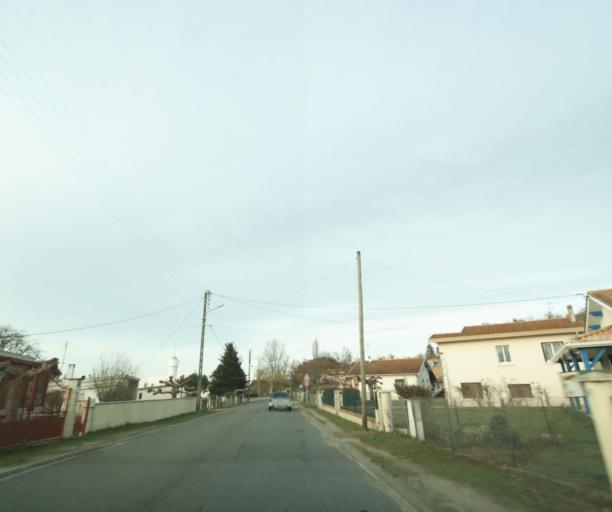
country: FR
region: Aquitaine
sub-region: Departement de la Gironde
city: Prechac
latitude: 44.2891
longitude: -0.2578
